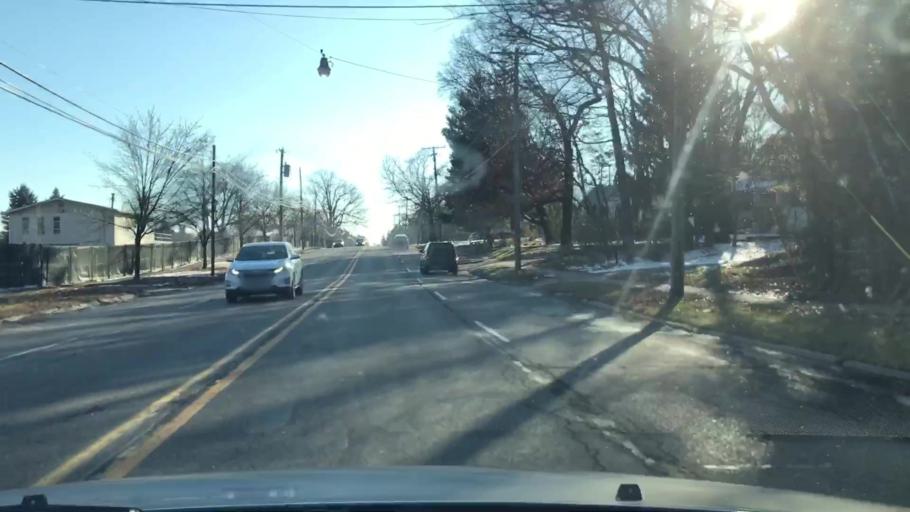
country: US
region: Michigan
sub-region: Oakland County
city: Royal Oak
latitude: 42.5089
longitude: -83.1420
